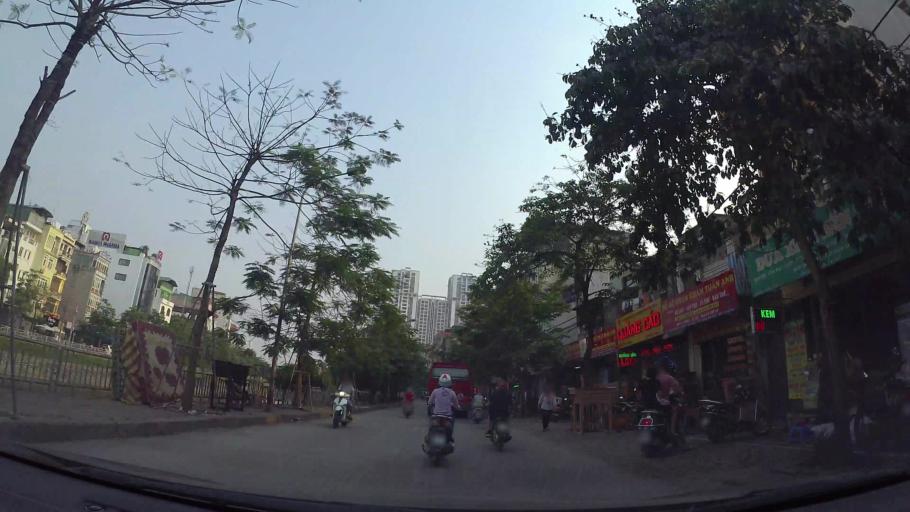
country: VN
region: Ha Noi
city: Thanh Xuan
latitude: 20.9891
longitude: 105.8130
